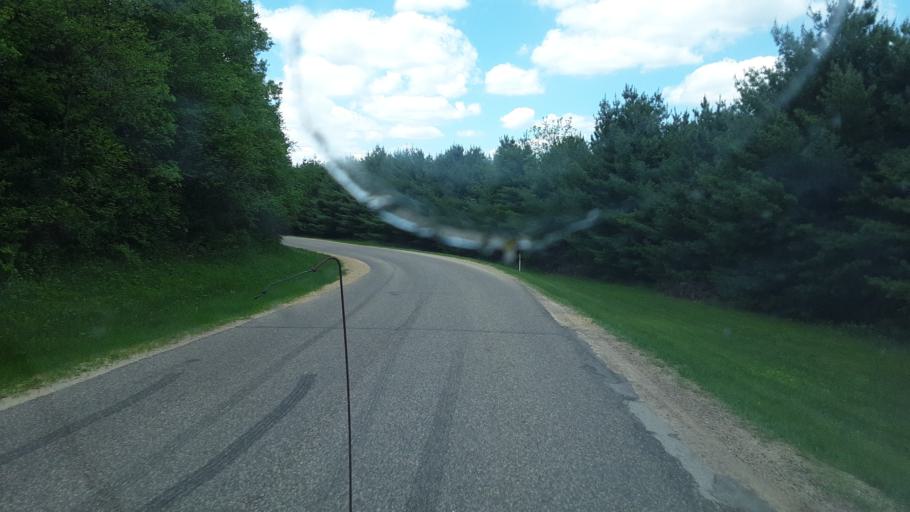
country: US
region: Wisconsin
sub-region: Sauk County
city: Reedsburg
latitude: 43.5637
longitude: -89.9963
